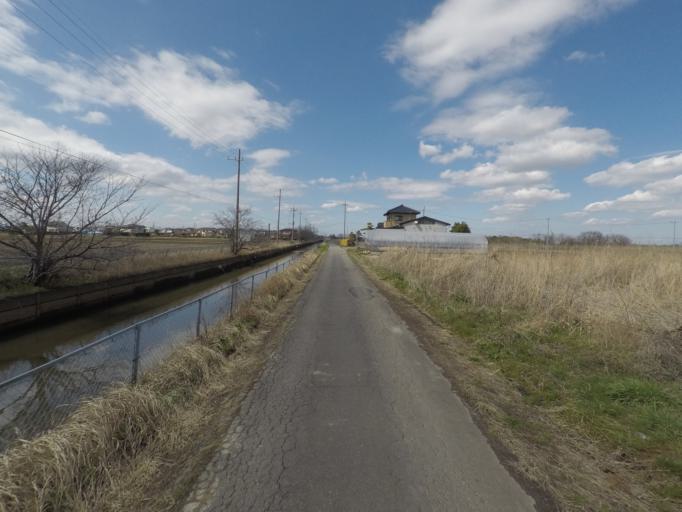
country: JP
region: Ibaraki
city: Fujishiro
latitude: 35.9361
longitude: 140.1283
